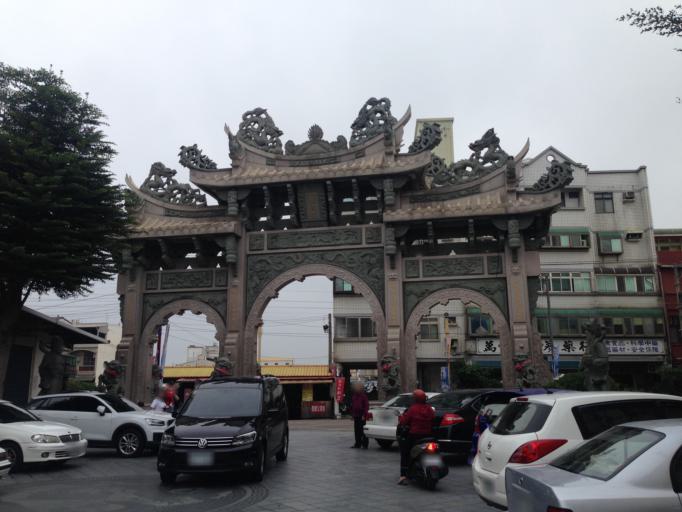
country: TW
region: Taiwan
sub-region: Miaoli
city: Miaoli
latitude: 24.6933
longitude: 120.8666
